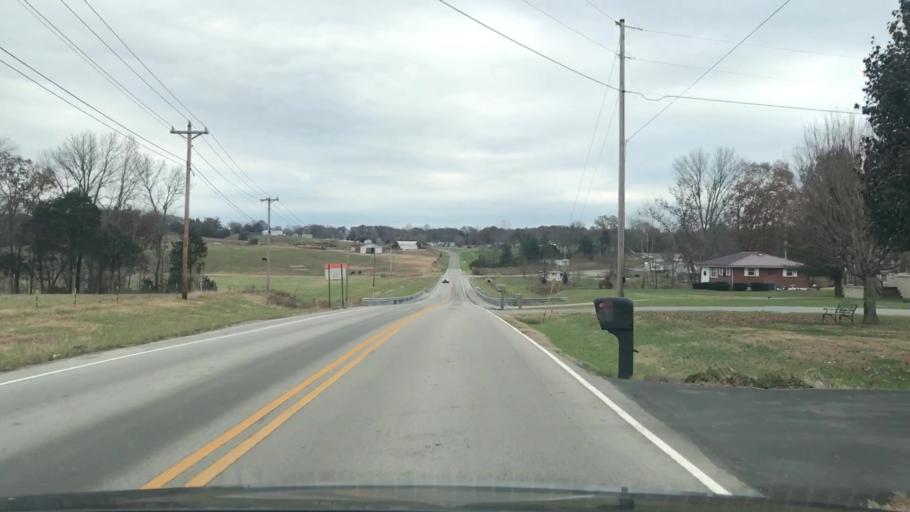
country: US
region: Kentucky
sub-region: Metcalfe County
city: Edmonton
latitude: 36.9398
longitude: -85.6236
